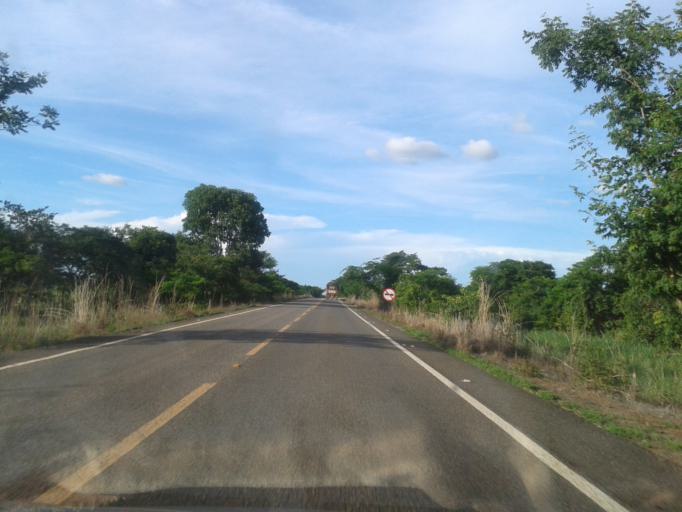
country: BR
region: Goias
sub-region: Sao Miguel Do Araguaia
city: Sao Miguel do Araguaia
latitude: -13.6983
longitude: -50.3320
